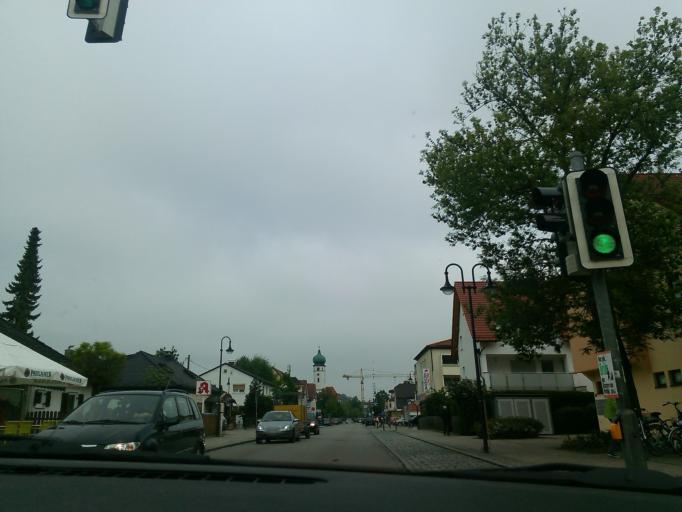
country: DE
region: Bavaria
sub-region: Upper Bavaria
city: Eichenau
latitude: 48.1697
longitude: 11.3227
